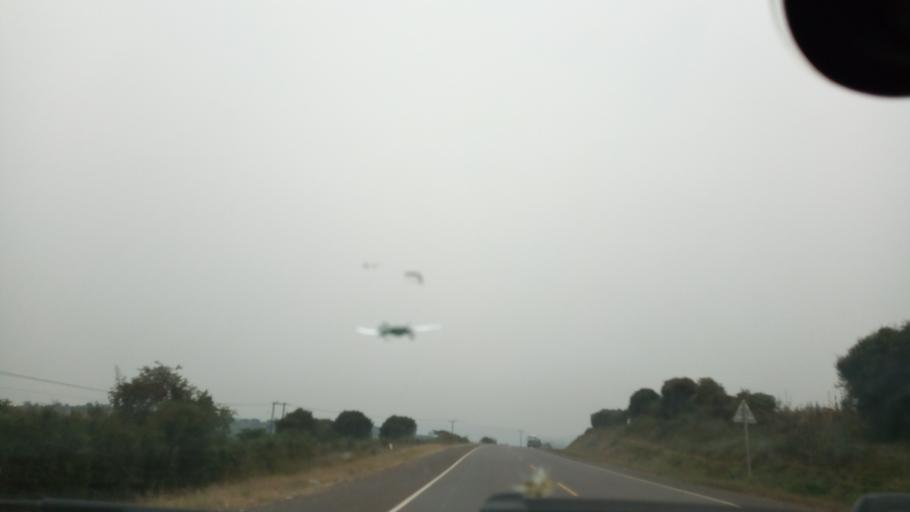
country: UG
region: Western Region
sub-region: Mbarara District
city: Mbarara
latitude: -0.7169
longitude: 30.7240
